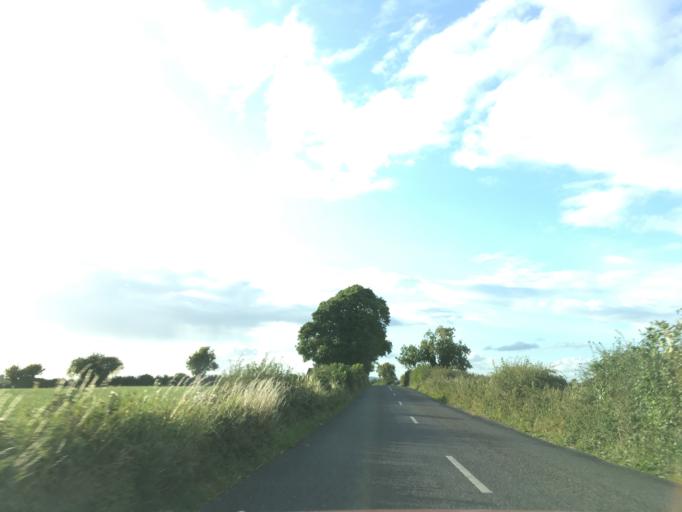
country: IE
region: Munster
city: Cashel
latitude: 52.4738
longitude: -7.9244
